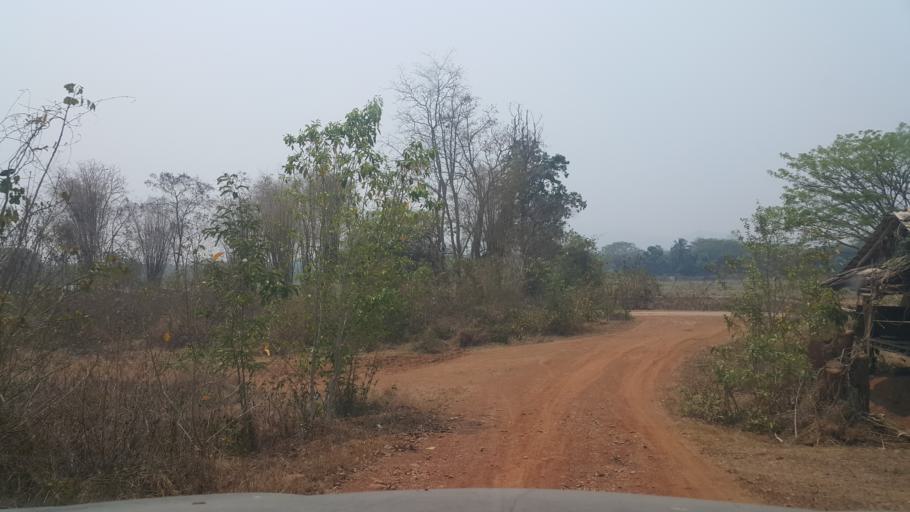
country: TH
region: Lampang
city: Sop Prap
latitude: 17.8854
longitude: 99.3179
